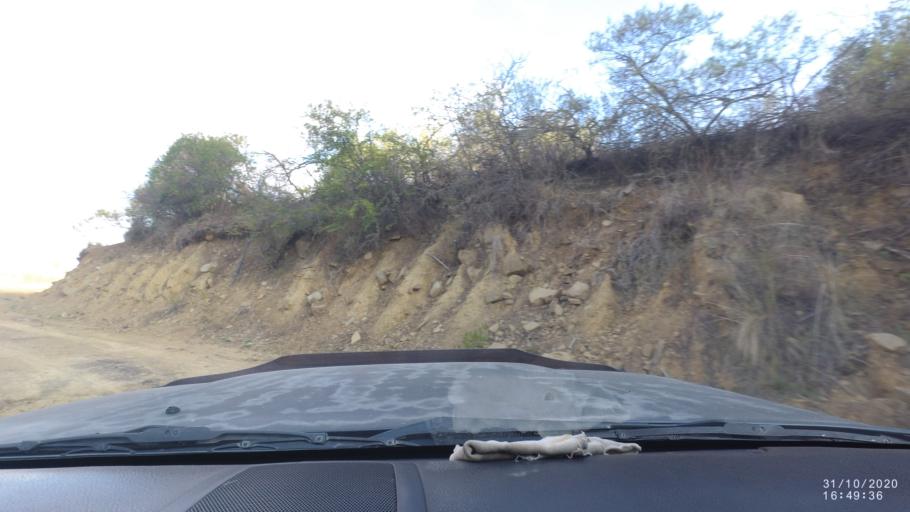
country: BO
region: Chuquisaca
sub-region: Provincia Zudanez
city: Mojocoya
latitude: -18.5073
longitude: -64.5717
